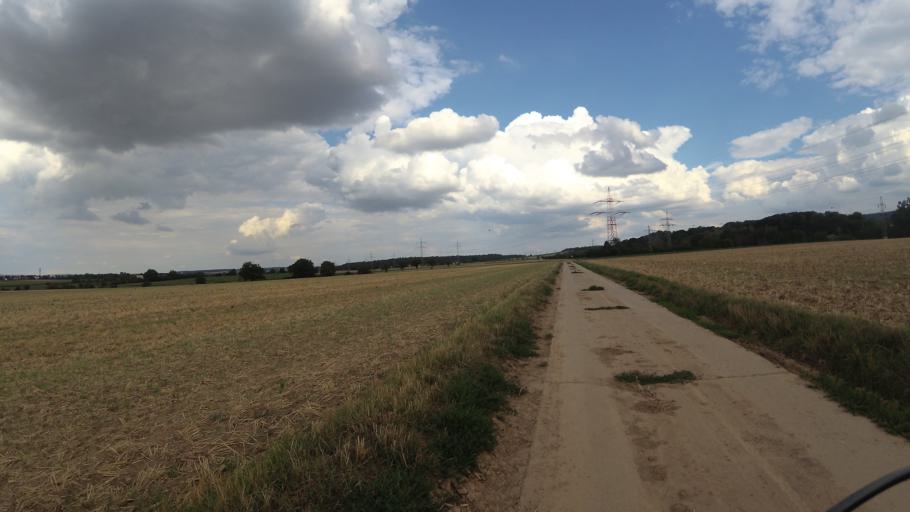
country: DE
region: Baden-Wuerttemberg
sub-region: Regierungsbezirk Stuttgart
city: Oedheim
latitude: 49.2209
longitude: 9.2478
